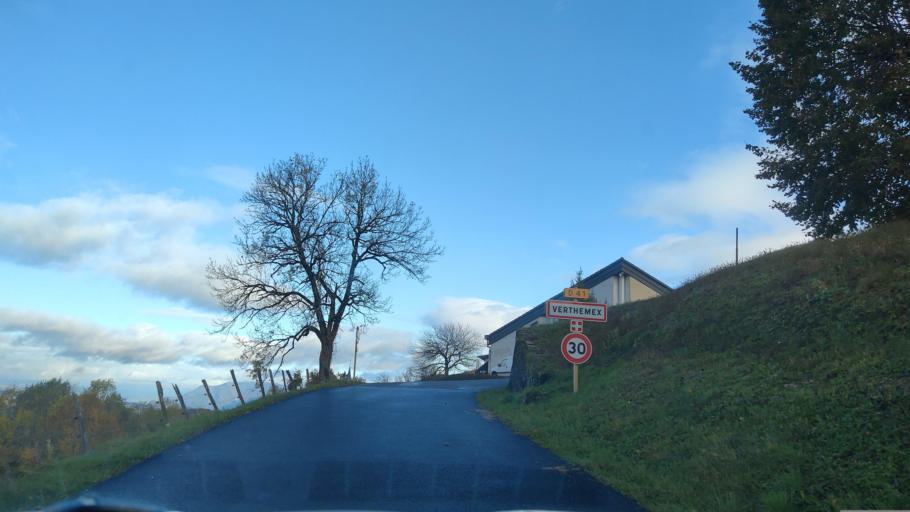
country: FR
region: Rhone-Alpes
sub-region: Departement de la Savoie
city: Novalaise
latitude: 45.6285
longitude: 5.7889
